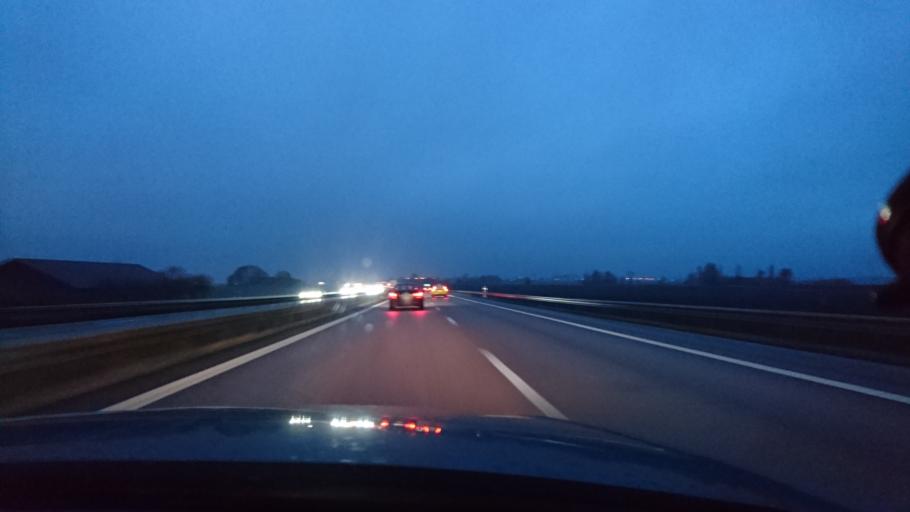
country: SE
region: Skane
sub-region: Helsingborg
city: Glumslov
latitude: 55.9566
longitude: 12.8033
